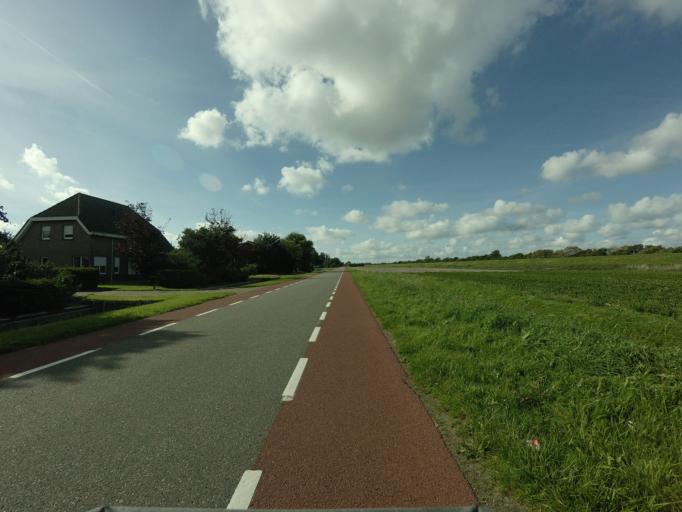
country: NL
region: North Holland
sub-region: Gemeente Den Helder
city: Den Helder
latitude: 52.9007
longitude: 4.8291
